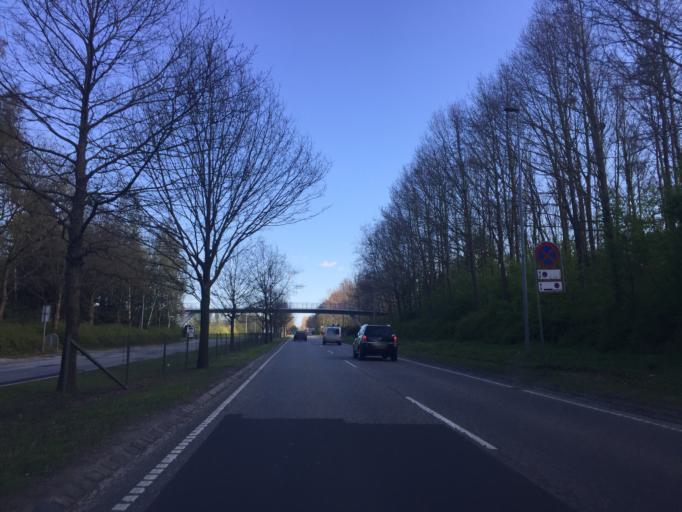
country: DK
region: South Denmark
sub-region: Odense Kommune
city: Neder Holluf
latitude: 55.3698
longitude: 10.4493
